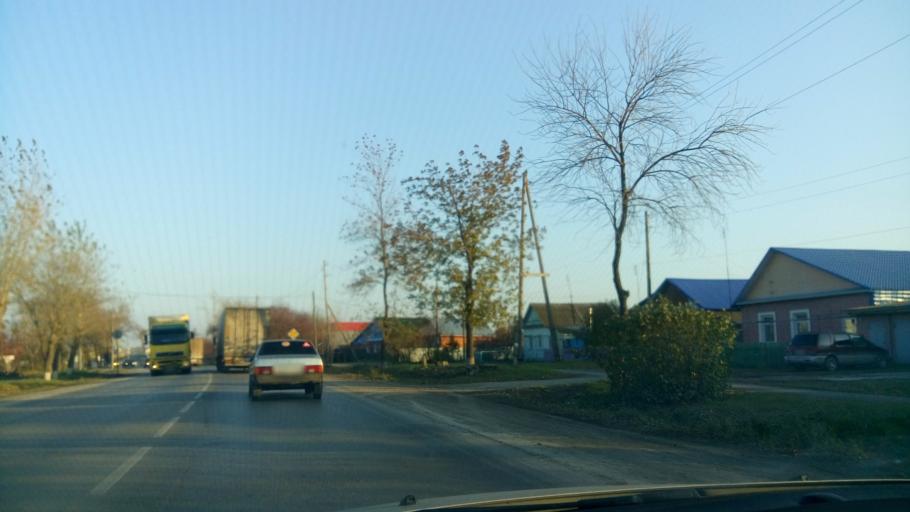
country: RU
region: Sverdlovsk
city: Bogdanovich
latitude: 56.7657
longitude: 62.0610
